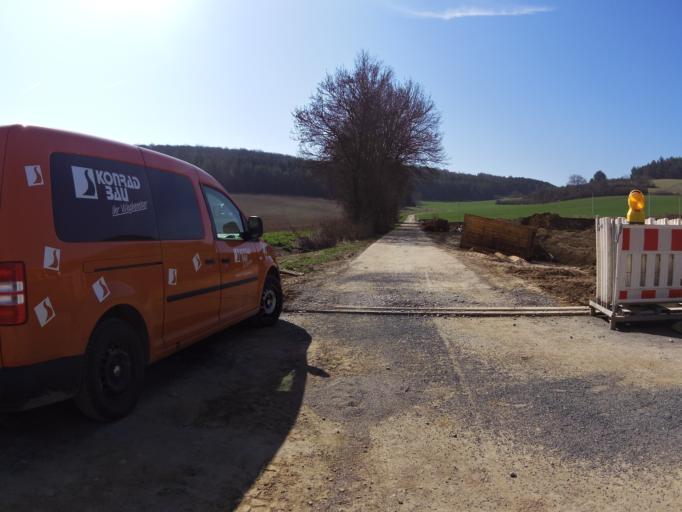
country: DE
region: Bavaria
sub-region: Regierungsbezirk Unterfranken
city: Erlabrunn
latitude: 49.8569
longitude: 9.8182
